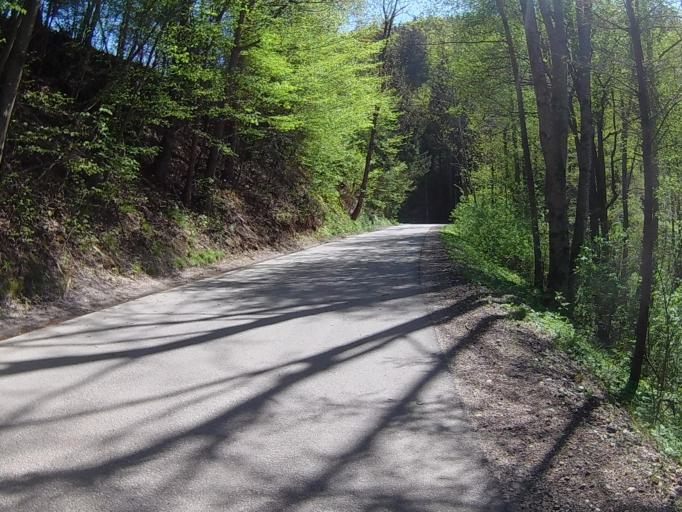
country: SI
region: Ruse
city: Ruse
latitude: 46.5272
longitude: 15.5104
